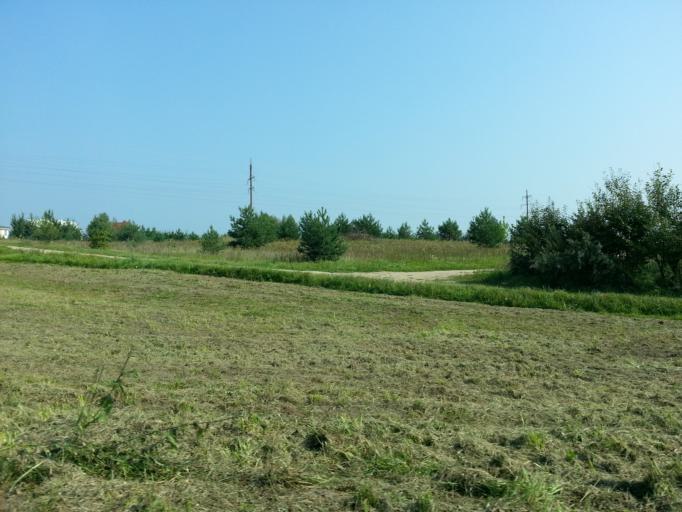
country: LT
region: Vilnius County
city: Justiniskes
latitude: 54.7245
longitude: 25.1961
